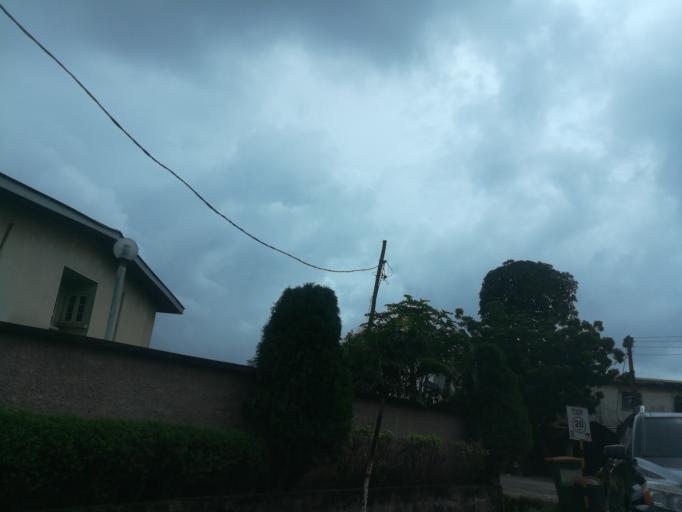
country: NG
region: Lagos
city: Ikeja
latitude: 6.6152
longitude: 3.3468
